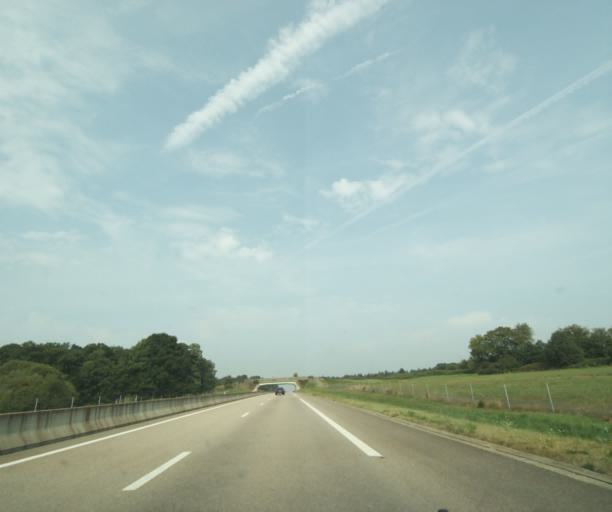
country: FR
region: Lower Normandy
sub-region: Departement du Calvados
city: Falaise
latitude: 48.8392
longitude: -0.1590
